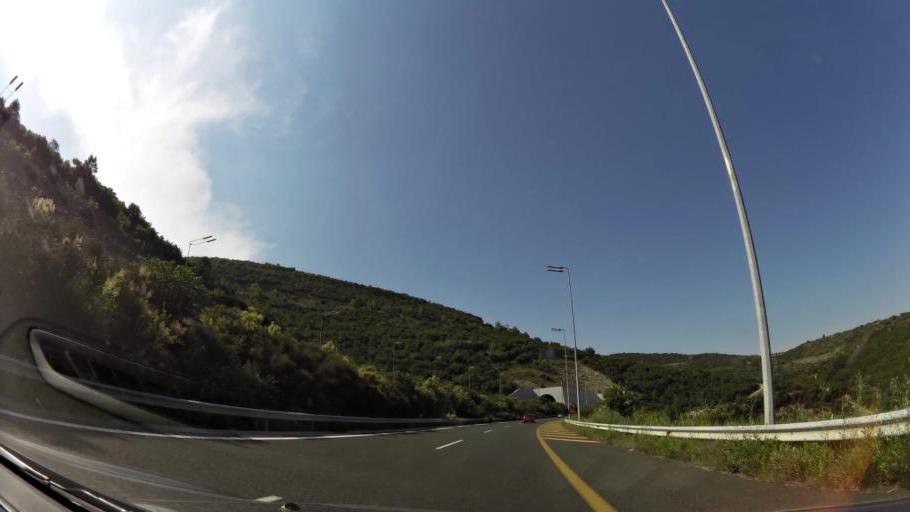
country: GR
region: Central Macedonia
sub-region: Nomos Imathias
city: Rizomata
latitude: 40.4360
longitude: 22.1802
